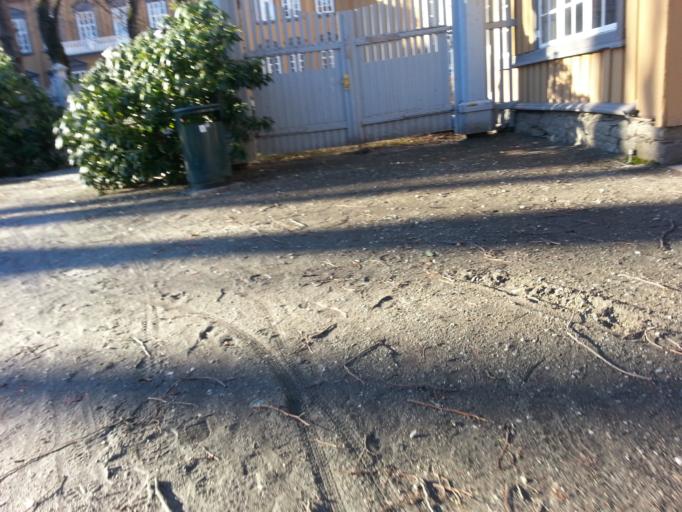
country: NO
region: Sor-Trondelag
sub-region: Trondheim
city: Trondheim
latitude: 63.4318
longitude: 10.3959
